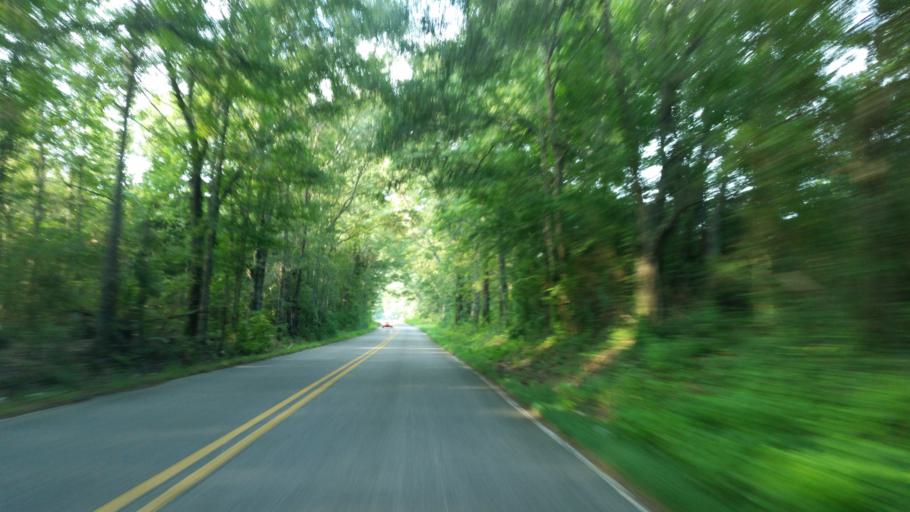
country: US
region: Alabama
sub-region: Escambia County
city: Atmore
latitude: 30.9930
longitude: -87.5712
